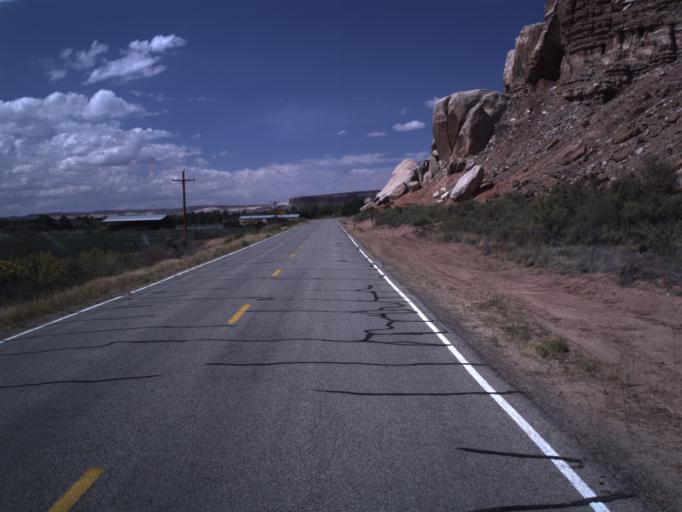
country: US
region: Utah
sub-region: San Juan County
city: Blanding
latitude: 37.2845
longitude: -109.5353
